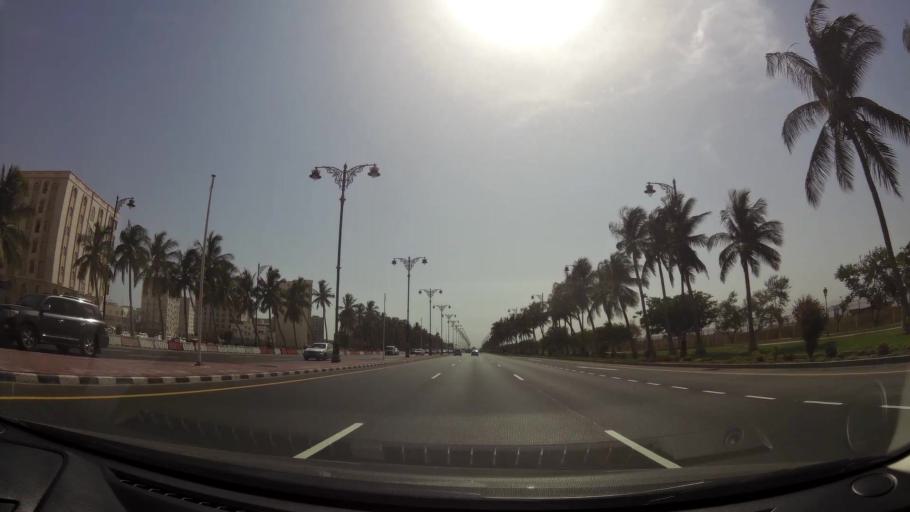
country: OM
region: Zufar
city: Salalah
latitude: 17.0237
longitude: 54.0984
